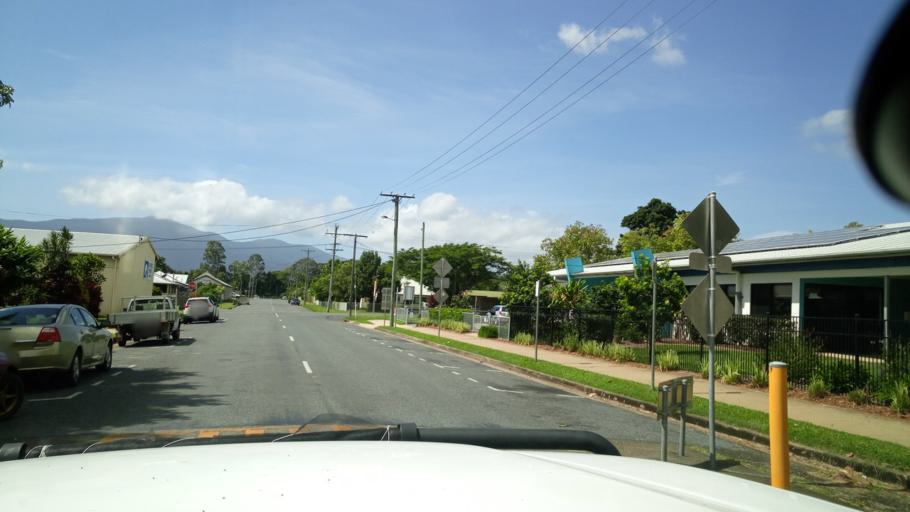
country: AU
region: Queensland
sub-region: Cairns
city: Woree
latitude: -17.0892
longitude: 145.7845
